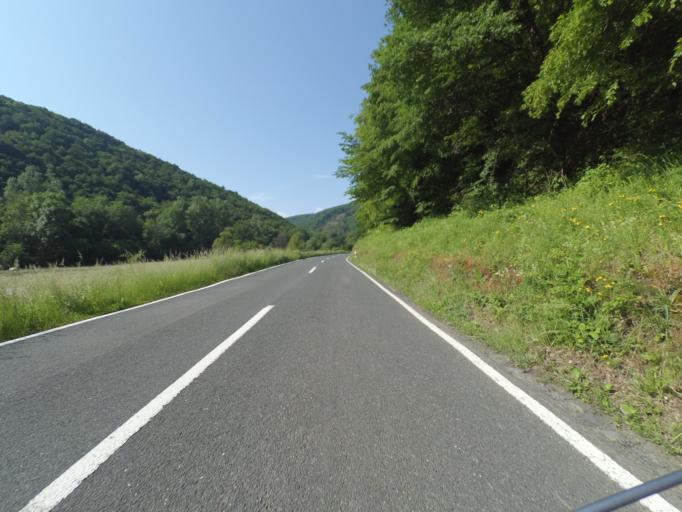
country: DE
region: Rheinland-Pfalz
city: Pommern
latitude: 50.1550
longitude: 7.2798
